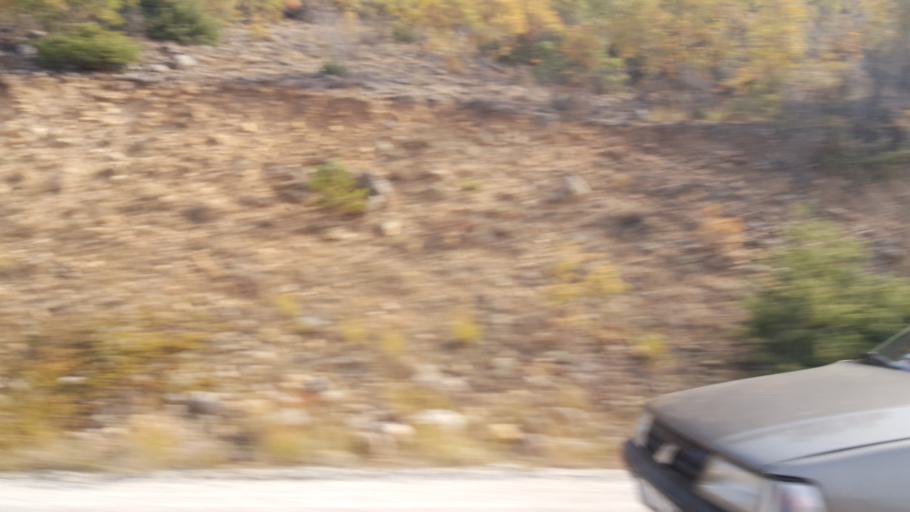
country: TR
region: Eskisehir
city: Mihaliccik
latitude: 39.9766
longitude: 31.3814
